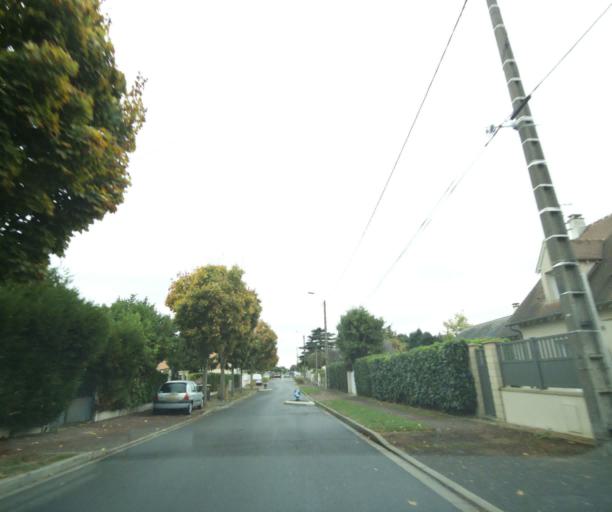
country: FR
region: Centre
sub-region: Departement d'Eure-et-Loir
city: Vernouillet
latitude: 48.7264
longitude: 1.3687
